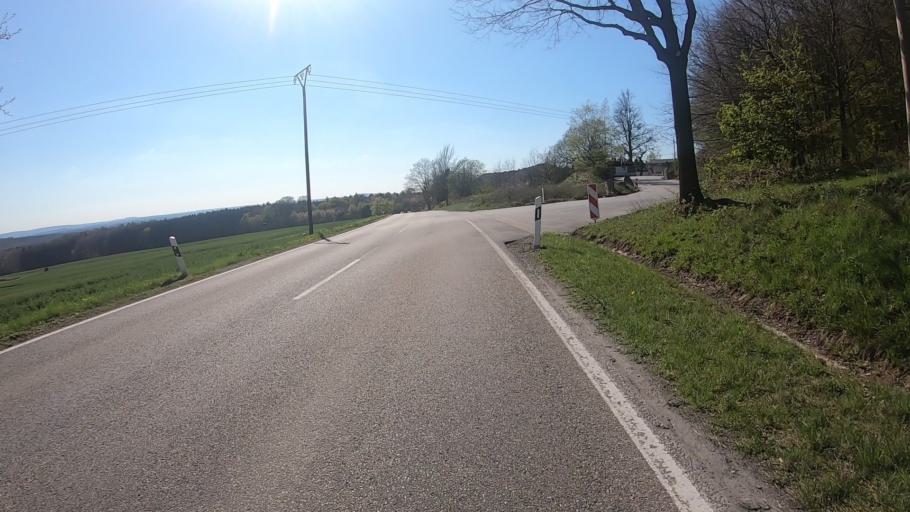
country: DE
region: Rheinland-Pfalz
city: Hartenfels
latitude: 50.5781
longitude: 7.7716
